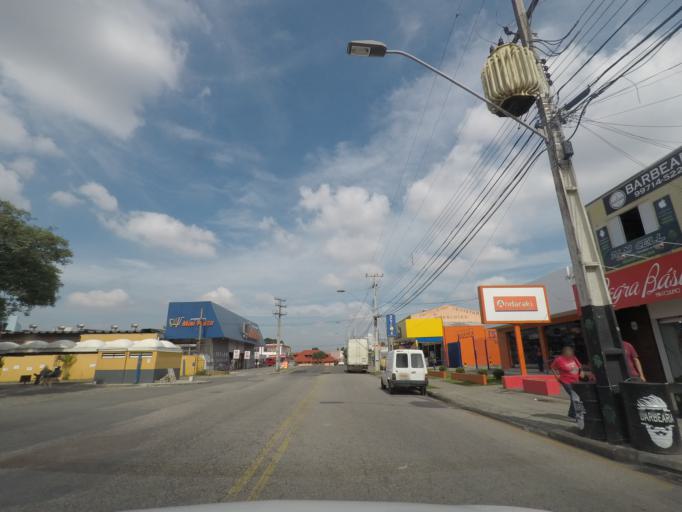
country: BR
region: Parana
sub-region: Pinhais
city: Pinhais
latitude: -25.4690
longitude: -49.2086
